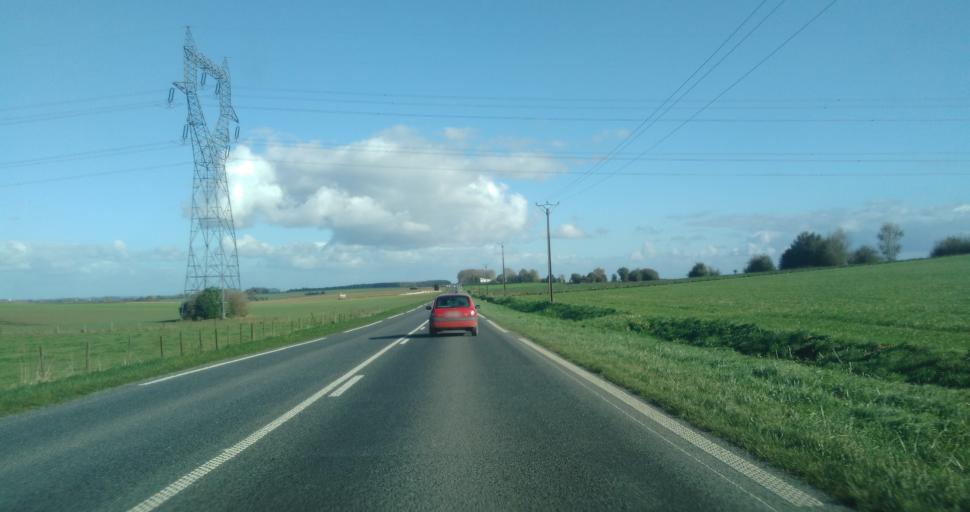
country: FR
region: Nord-Pas-de-Calais
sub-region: Departement du Pas-de-Calais
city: Beaumetz-les-Loges
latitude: 50.2221
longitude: 2.5937
